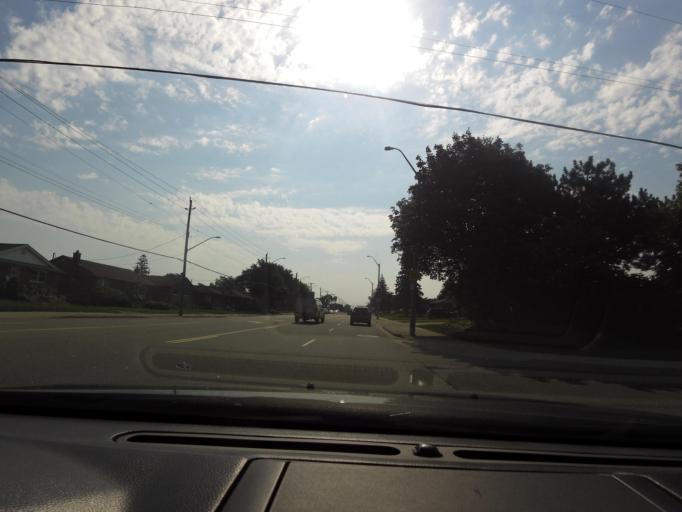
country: CA
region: Ontario
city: Hamilton
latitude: 43.2245
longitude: -79.8650
